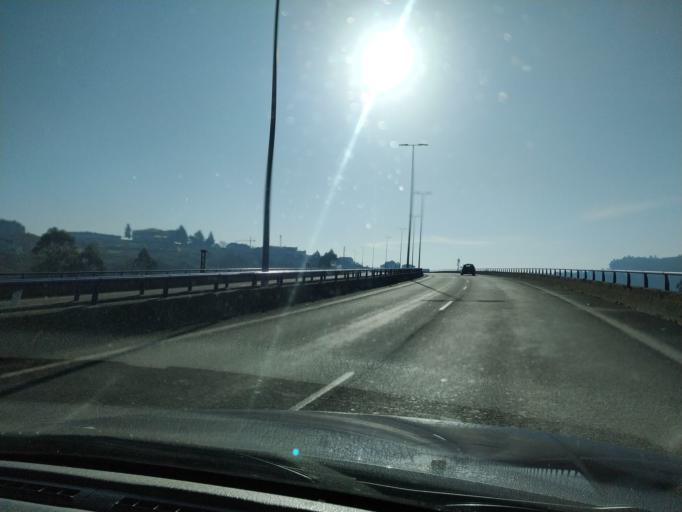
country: ES
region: Galicia
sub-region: Provincia da Coruna
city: Santiago de Compostela
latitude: 42.8643
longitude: -8.5518
